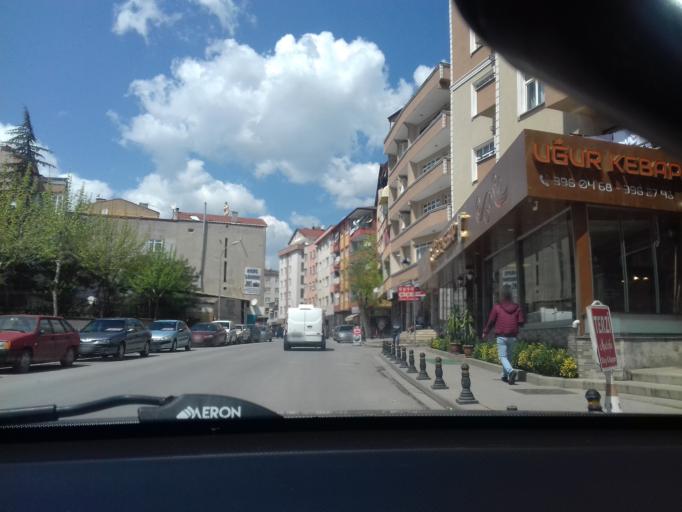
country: TR
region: Istanbul
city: Pendik
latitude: 40.8710
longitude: 29.2725
